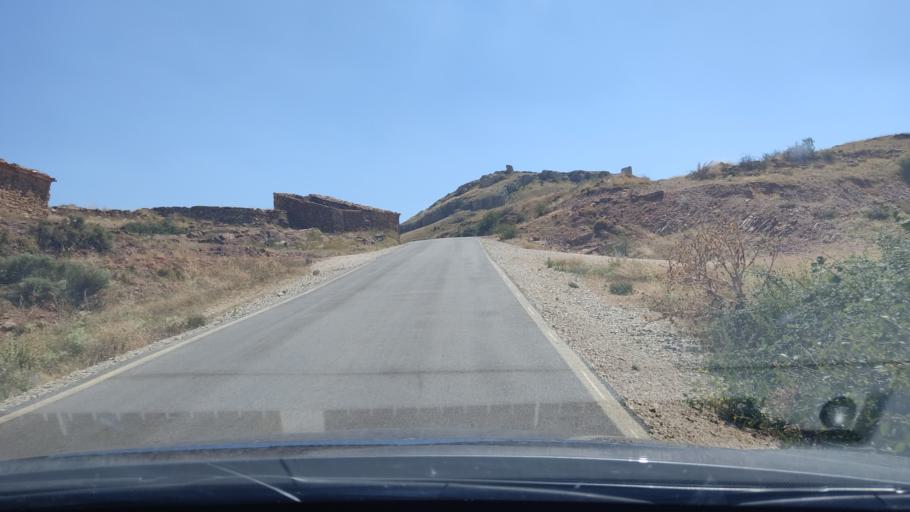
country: ES
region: Aragon
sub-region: Provincia de Teruel
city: Monforte de Moyuela
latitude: 41.0585
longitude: -1.0189
